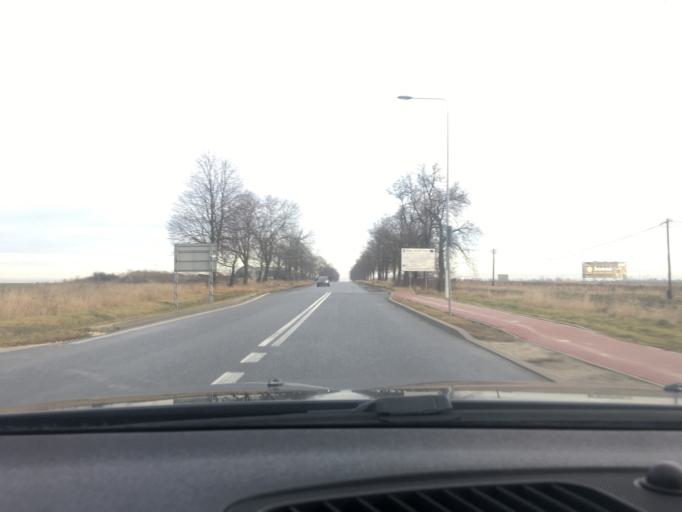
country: PL
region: Swietokrzyskie
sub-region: Powiat jedrzejowski
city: Jedrzejow
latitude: 50.6491
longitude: 20.3170
